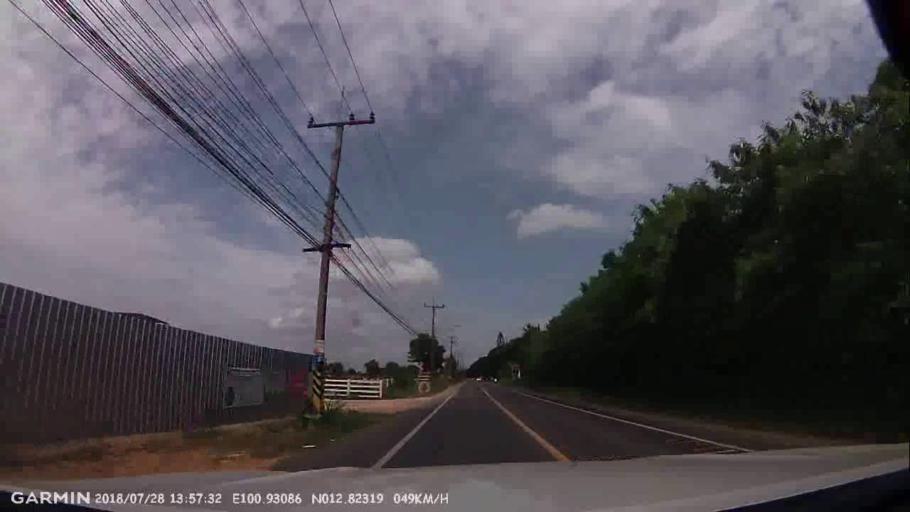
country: TH
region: Chon Buri
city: Phatthaya
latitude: 12.8232
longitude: 100.9308
